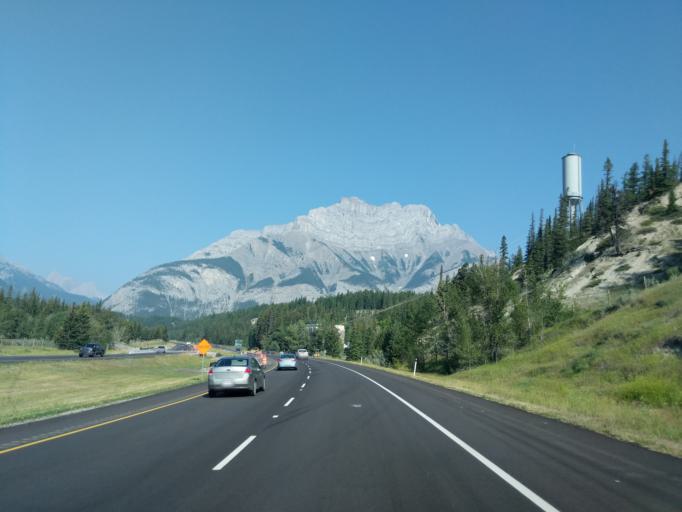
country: CA
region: Alberta
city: Banff
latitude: 51.1991
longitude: -115.4996
